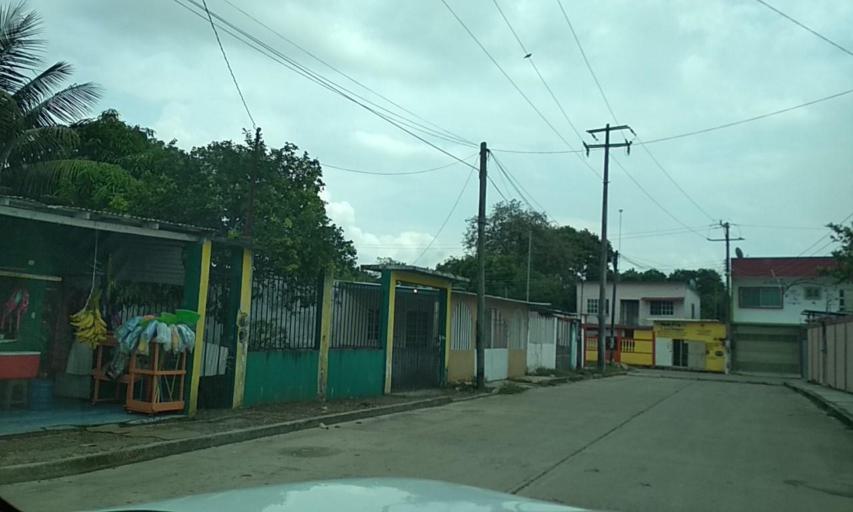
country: MX
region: Veracruz
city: Las Choapas
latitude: 17.8976
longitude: -94.0987
